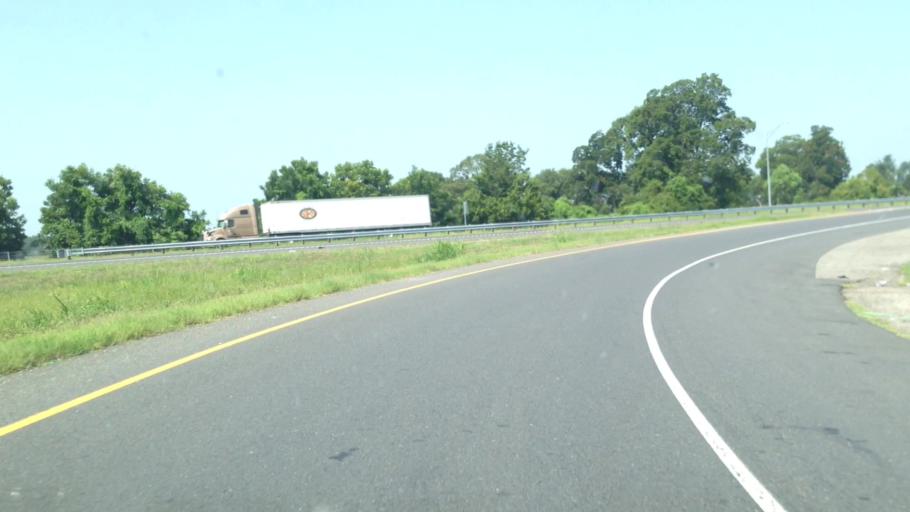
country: US
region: Louisiana
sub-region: Madison Parish
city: Tallulah
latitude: 32.3938
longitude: -91.2011
